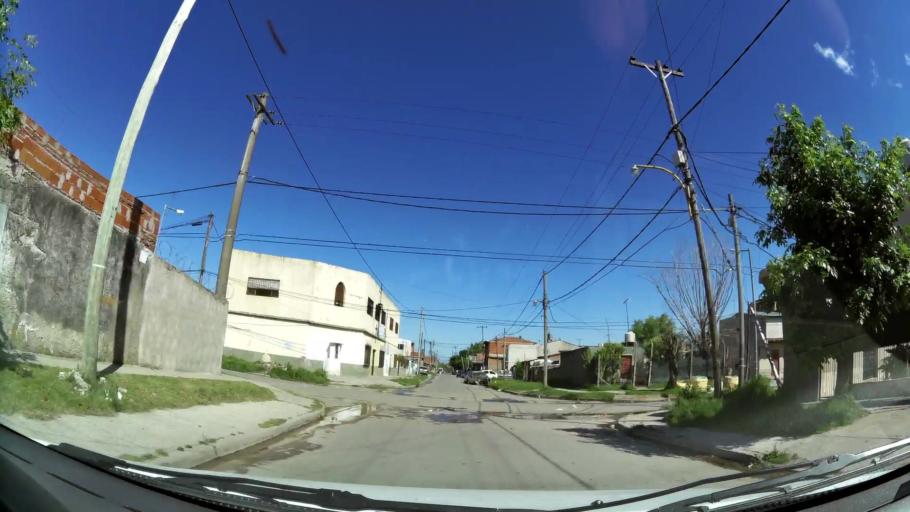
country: AR
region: Buenos Aires
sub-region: Partido de Tigre
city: Tigre
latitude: -34.5079
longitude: -58.5856
